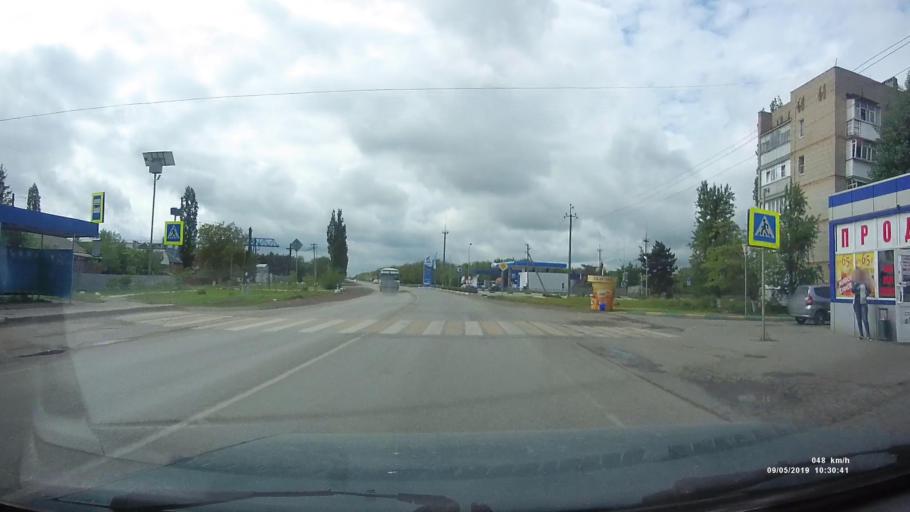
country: RU
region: Rostov
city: Azov
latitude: 47.0882
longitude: 39.4291
